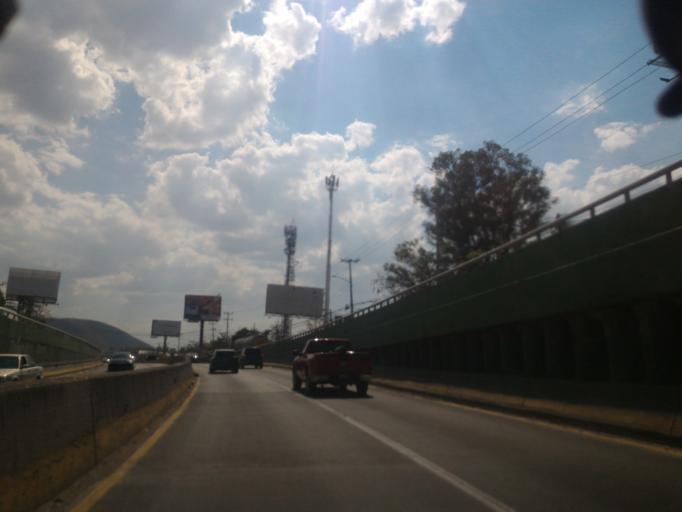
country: MX
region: Jalisco
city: Nicolas R Casillas
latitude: 20.5461
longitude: -103.4721
